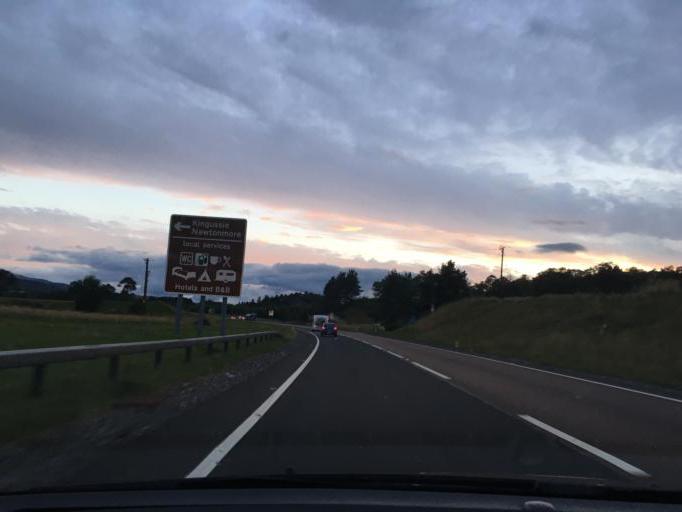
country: GB
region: Scotland
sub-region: Highland
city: Kingussie
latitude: 57.0886
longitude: -4.0321
